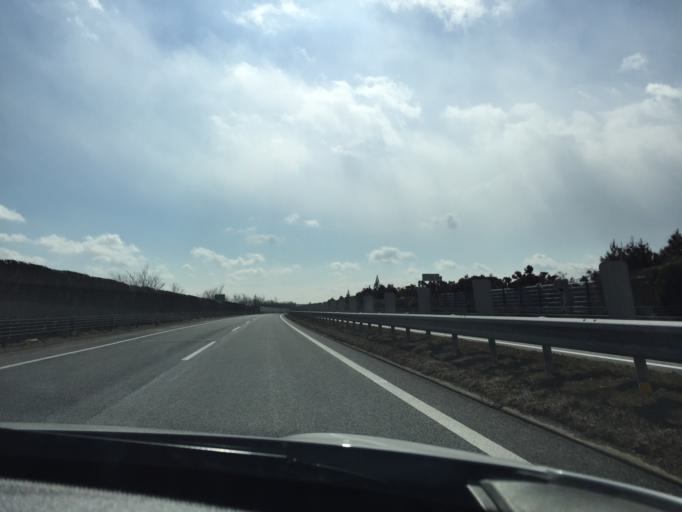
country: JP
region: Fukushima
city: Koriyama
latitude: 37.3860
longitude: 140.3124
